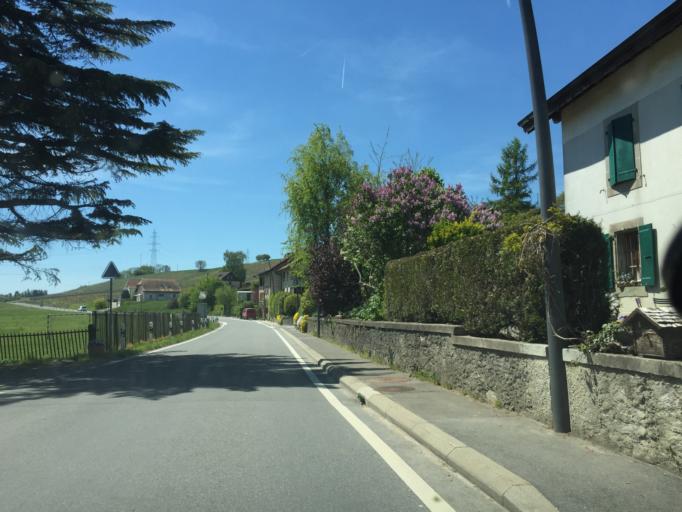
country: CH
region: Vaud
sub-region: Morges District
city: Apples
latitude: 46.5463
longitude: 6.4493
